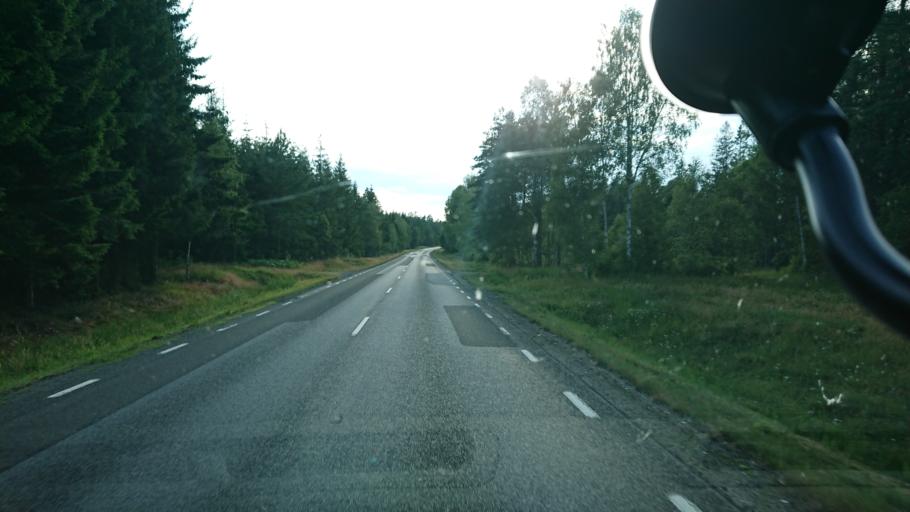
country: SE
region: Kronoberg
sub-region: Vaxjo Kommun
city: Braas
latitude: 57.0249
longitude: 14.9973
